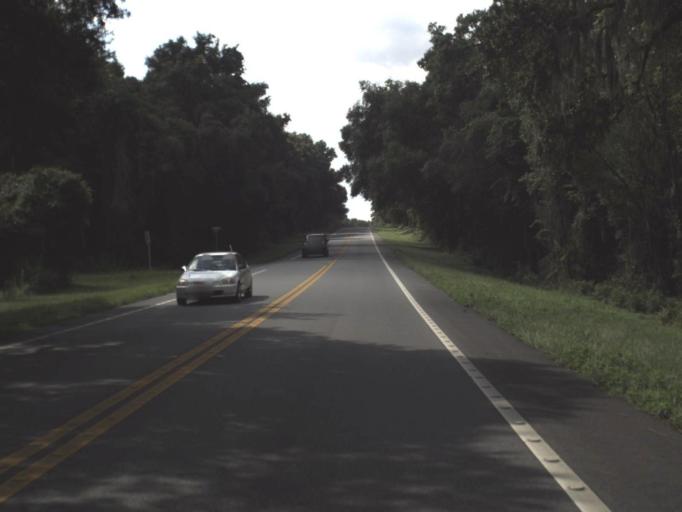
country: US
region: Florida
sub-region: Citrus County
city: Hernando
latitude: 28.9351
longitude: -82.3966
